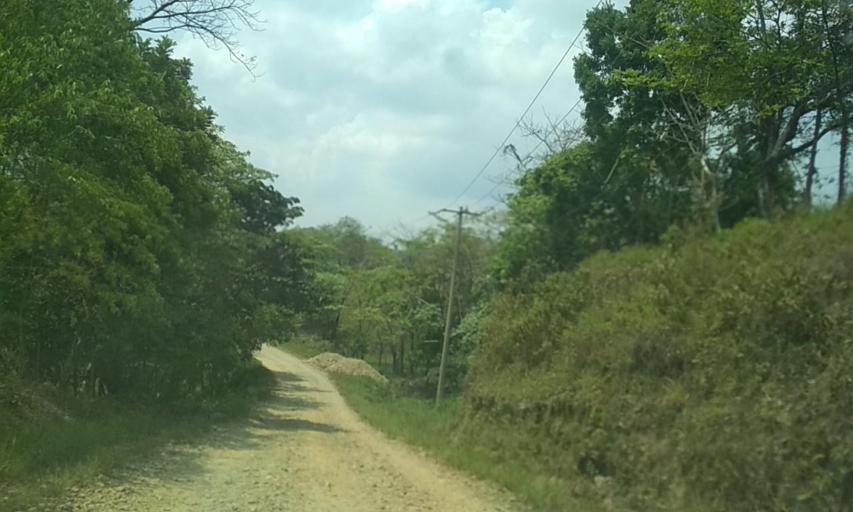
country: MX
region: Tabasco
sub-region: Huimanguillo
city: Francisco Rueda
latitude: 17.6159
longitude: -93.8129
